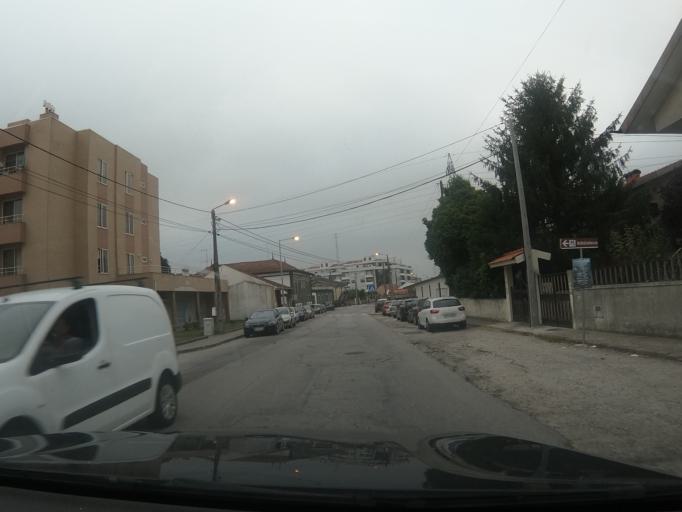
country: PT
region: Aveiro
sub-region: Santa Maria da Feira
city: Pacos de Brandao
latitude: 40.9845
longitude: -8.5985
